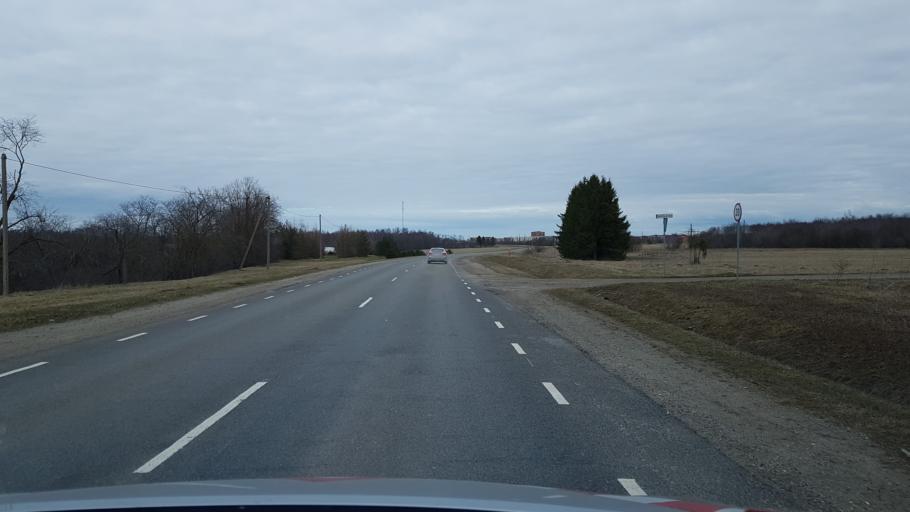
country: EE
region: Ida-Virumaa
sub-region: Sillamaee linn
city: Sillamae
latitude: 59.3805
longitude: 27.7653
